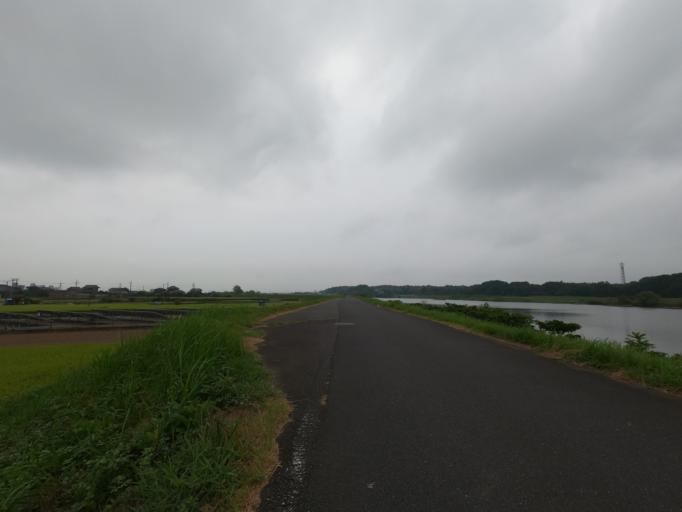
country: JP
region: Ibaraki
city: Moriya
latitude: 35.9340
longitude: 140.0435
